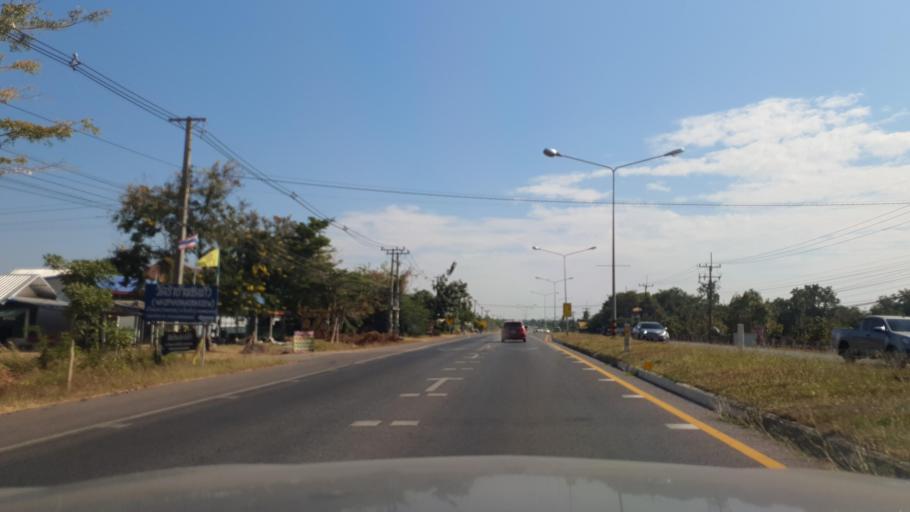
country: TH
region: Maha Sarakham
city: Chiang Yuen
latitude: 16.3742
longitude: 103.1553
